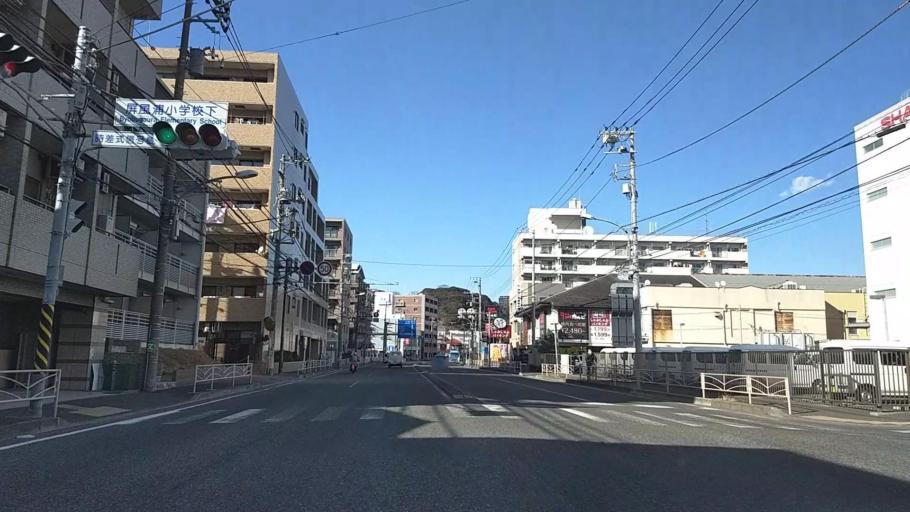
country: JP
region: Kanagawa
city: Yokohama
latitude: 35.3912
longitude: 139.6150
